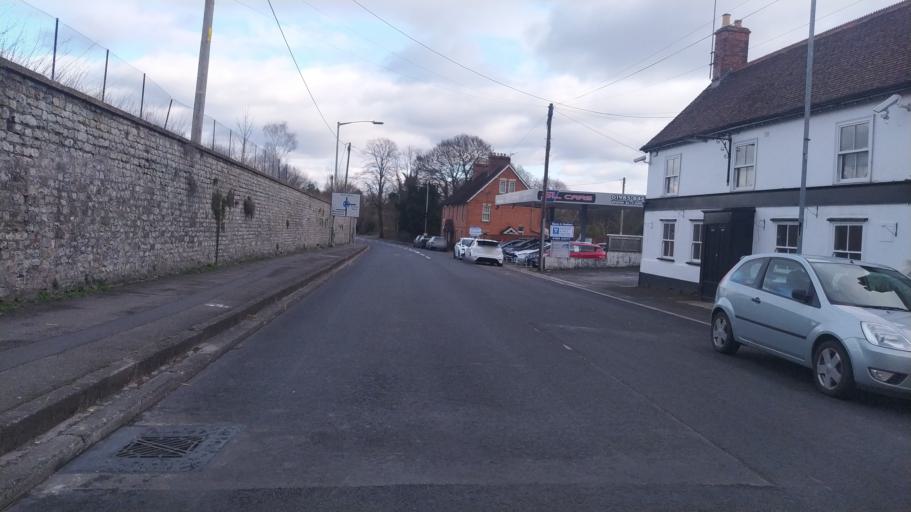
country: GB
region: England
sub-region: Wiltshire
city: Boreham
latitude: 51.1981
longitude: -2.1603
